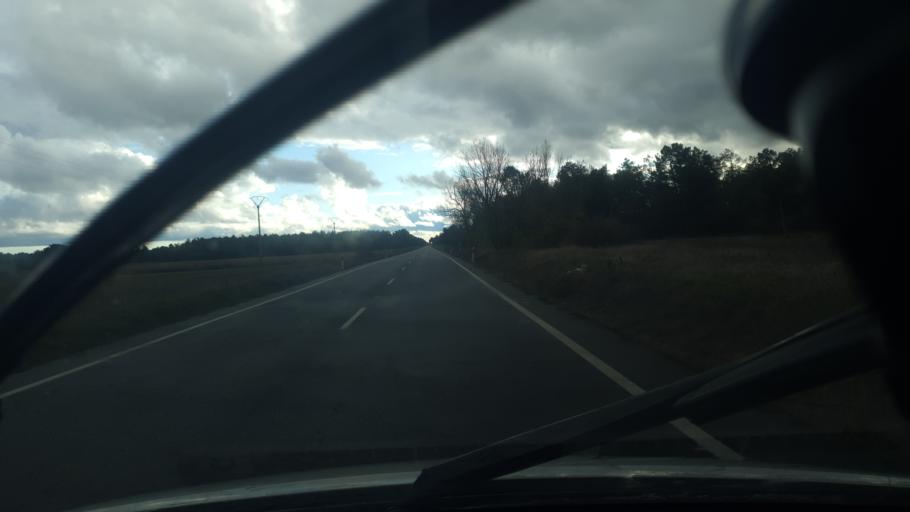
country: ES
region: Castille and Leon
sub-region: Provincia de Segovia
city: Samboal
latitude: 41.2802
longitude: -4.4140
